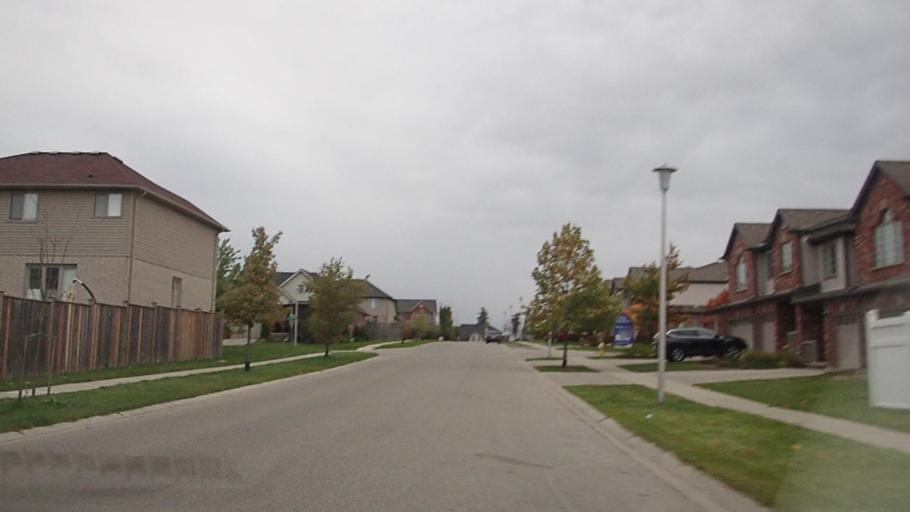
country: CA
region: Ontario
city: London
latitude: 43.0396
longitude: -81.2739
